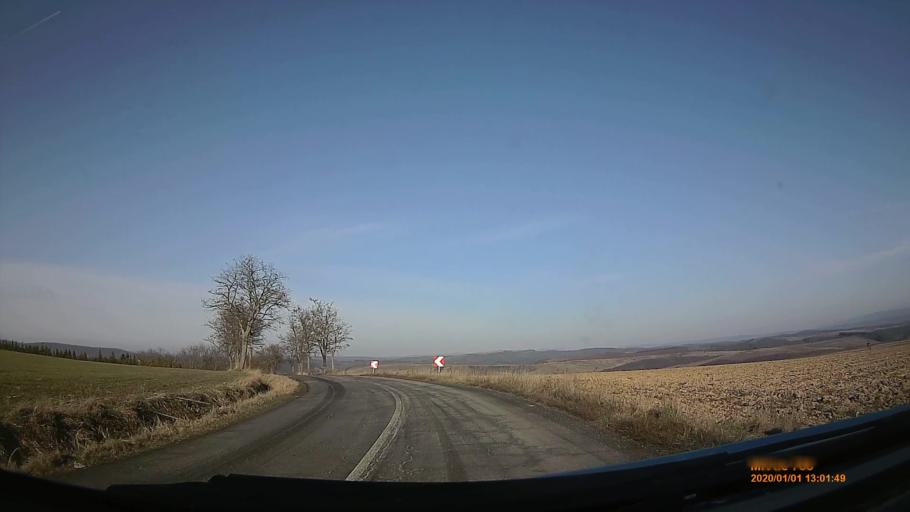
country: HU
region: Heves
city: Parad
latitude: 47.9310
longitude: 20.0249
